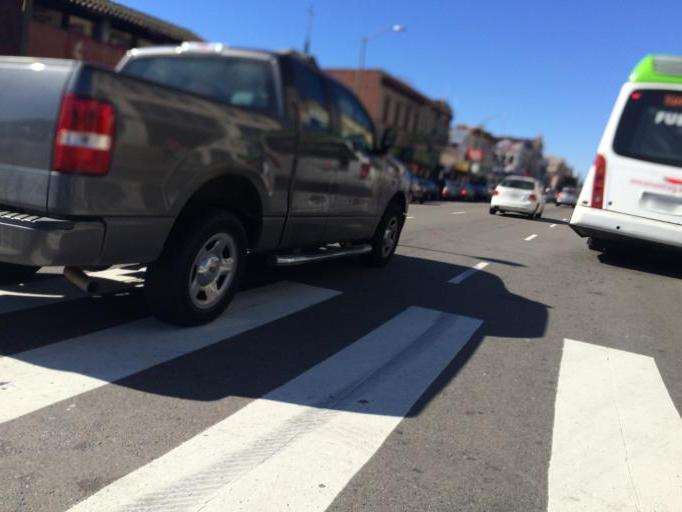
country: US
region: California
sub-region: Alameda County
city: Oakland
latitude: 37.7989
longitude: -122.2704
